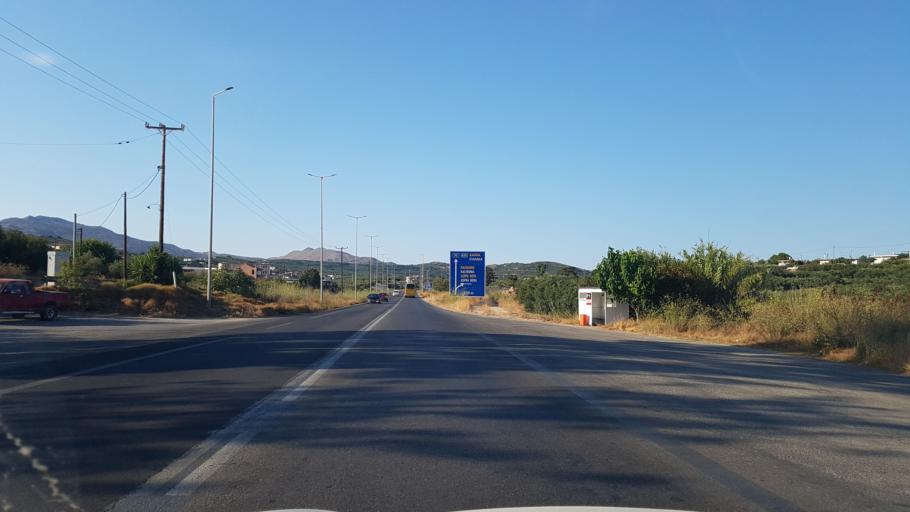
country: GR
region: Crete
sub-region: Nomos Chanias
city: Kolympari
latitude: 35.5240
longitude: 23.7474
